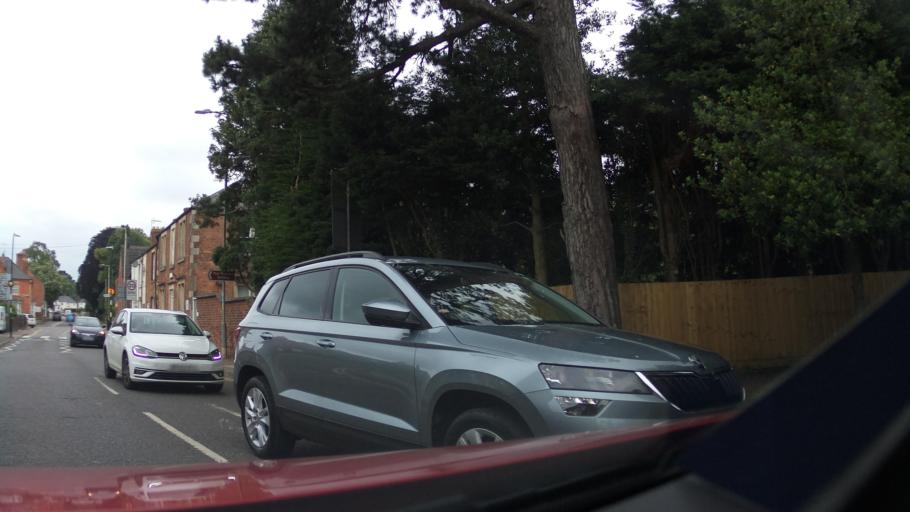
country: GB
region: England
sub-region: District of Rutland
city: Oakham
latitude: 52.6710
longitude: -0.7348
